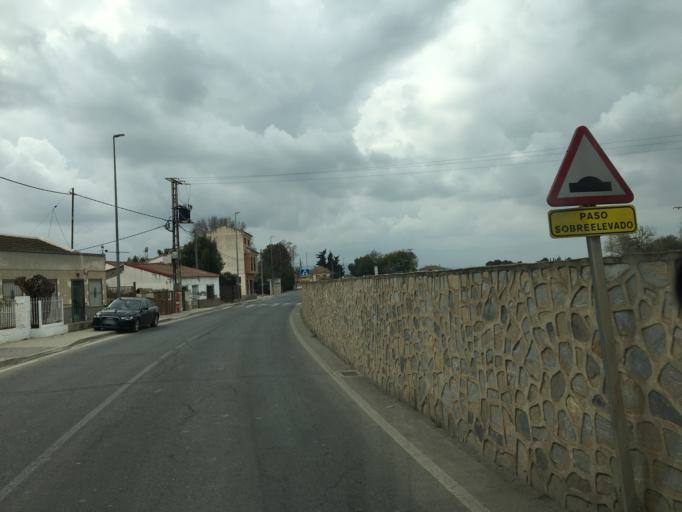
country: ES
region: Murcia
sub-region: Murcia
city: Beniel
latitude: 38.0359
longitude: -1.0129
